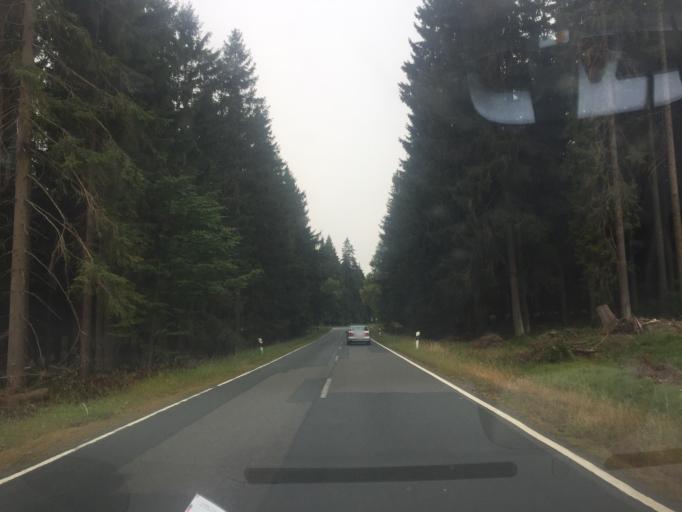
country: DE
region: Lower Saxony
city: Wieda
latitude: 51.6787
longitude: 10.6000
